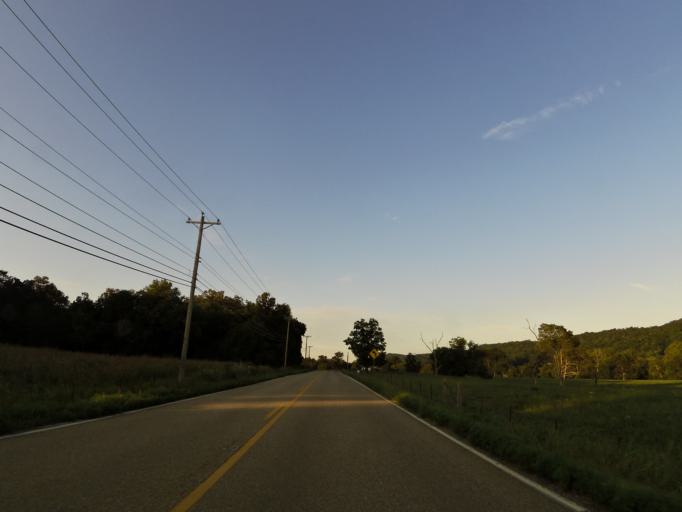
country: US
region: Tennessee
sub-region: Roane County
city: Midtown
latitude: 35.7722
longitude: -84.5866
